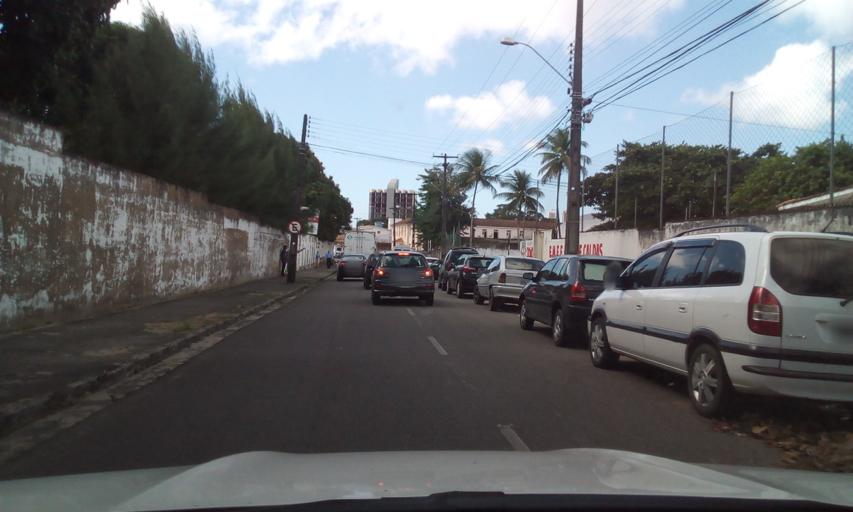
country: BR
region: Paraiba
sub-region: Joao Pessoa
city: Joao Pessoa
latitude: -7.1294
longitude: -34.8743
